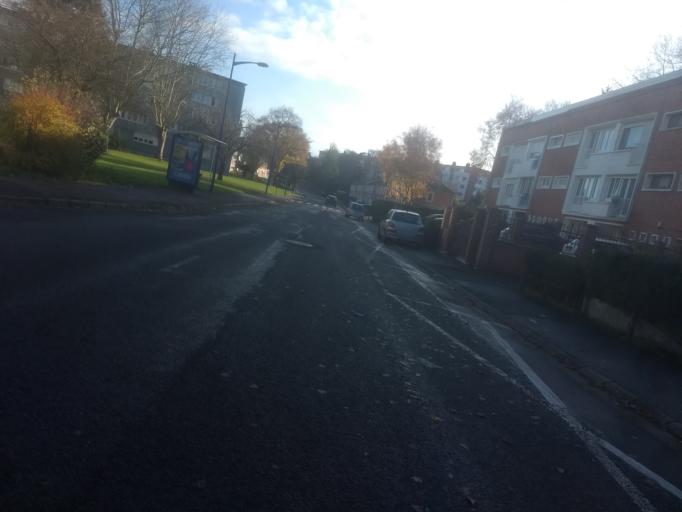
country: FR
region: Nord-Pas-de-Calais
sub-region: Departement du Pas-de-Calais
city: Anzin-Saint-Aubin
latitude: 50.3002
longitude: 2.7485
